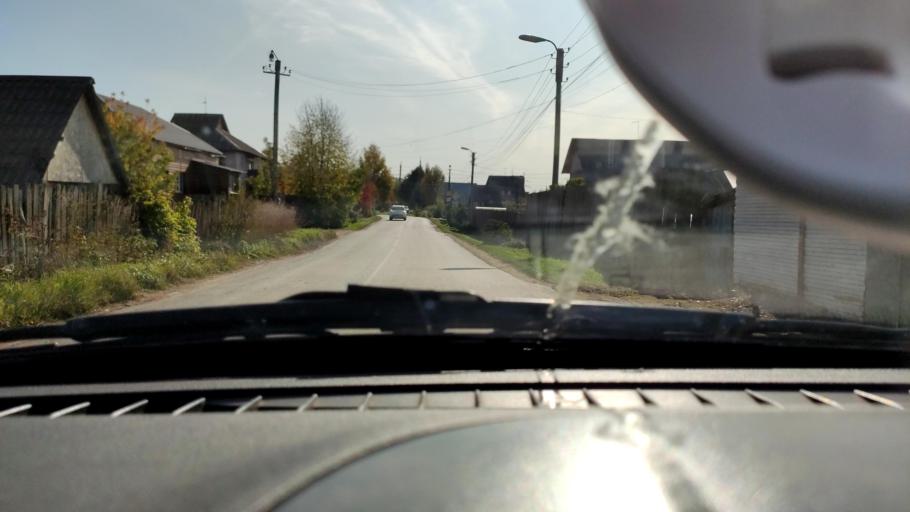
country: RU
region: Perm
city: Overyata
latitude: 58.0824
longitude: 55.8792
